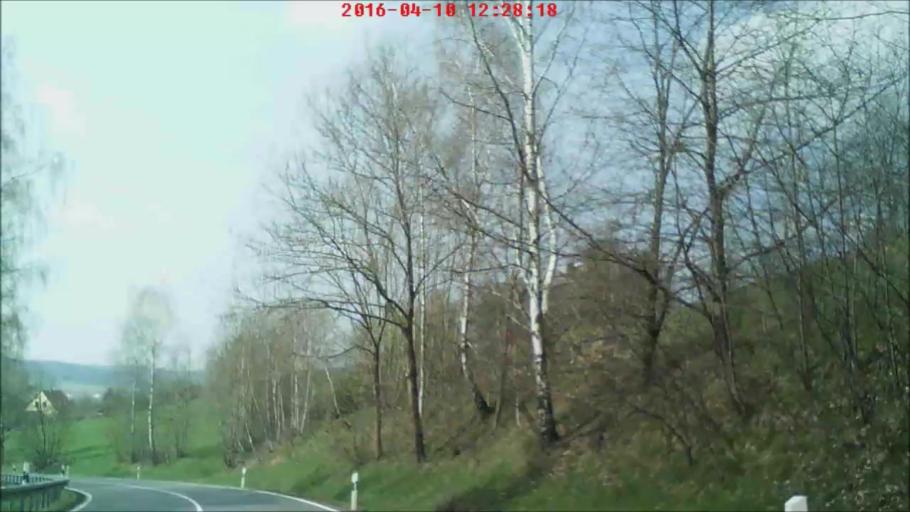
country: DE
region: Thuringia
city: Springstille
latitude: 50.6853
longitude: 10.5357
